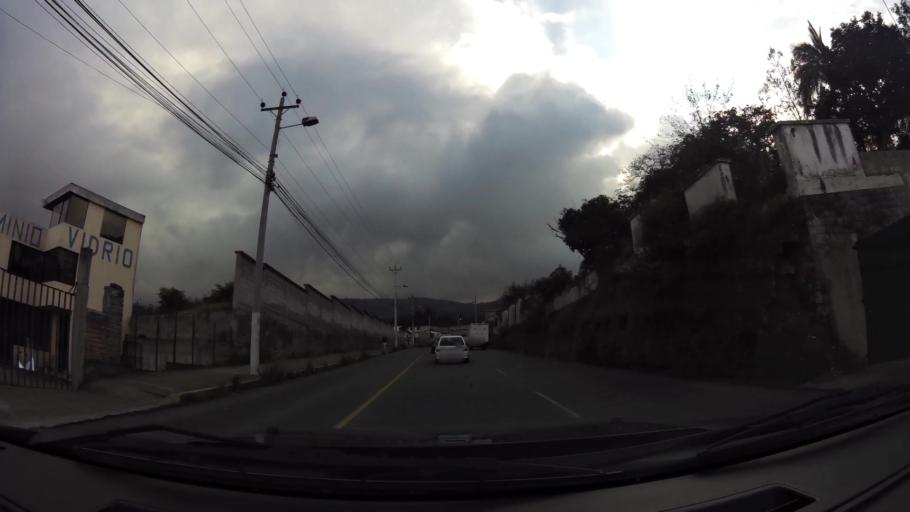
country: EC
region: Pichincha
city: Sangolqui
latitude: -0.2913
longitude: -78.4867
